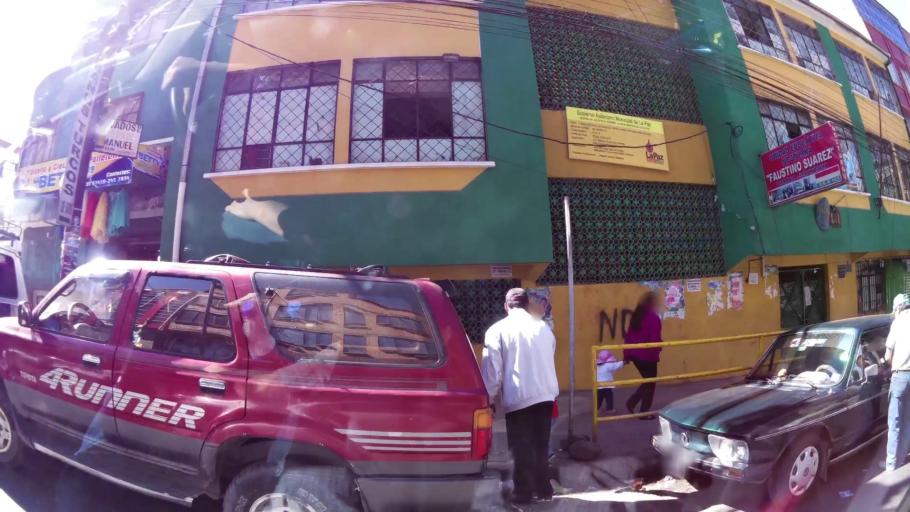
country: BO
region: La Paz
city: La Paz
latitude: -16.4943
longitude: -68.1529
